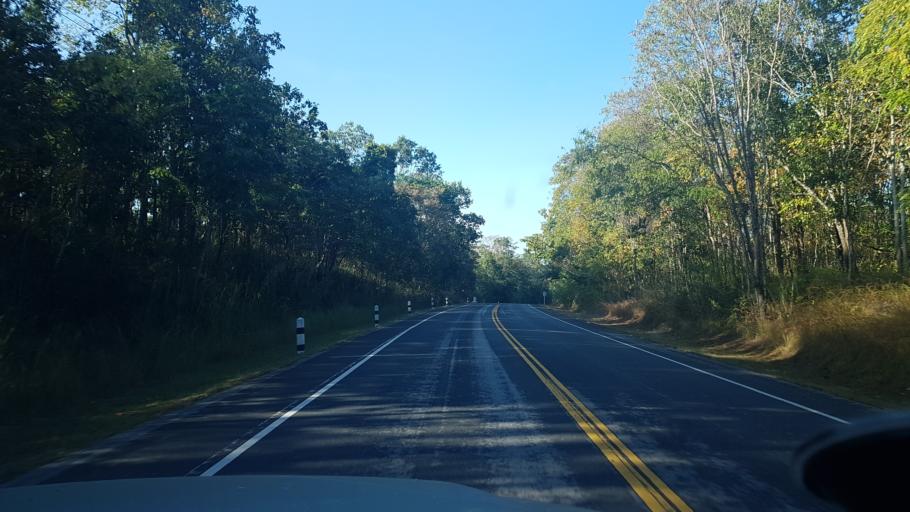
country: TH
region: Phetchabun
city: Lom Sak
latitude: 16.7412
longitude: 101.4460
